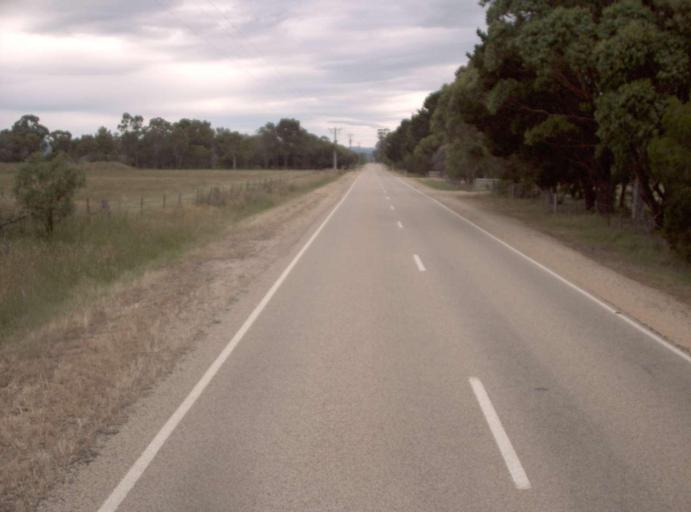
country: AU
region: Victoria
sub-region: East Gippsland
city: Bairnsdale
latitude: -37.8594
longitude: 147.5637
